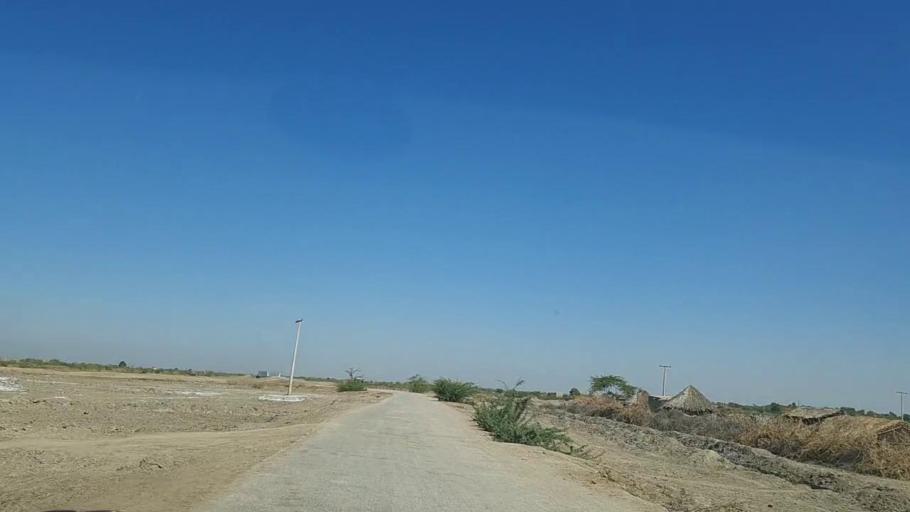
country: PK
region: Sindh
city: Dhoro Naro
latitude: 25.4734
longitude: 69.5264
